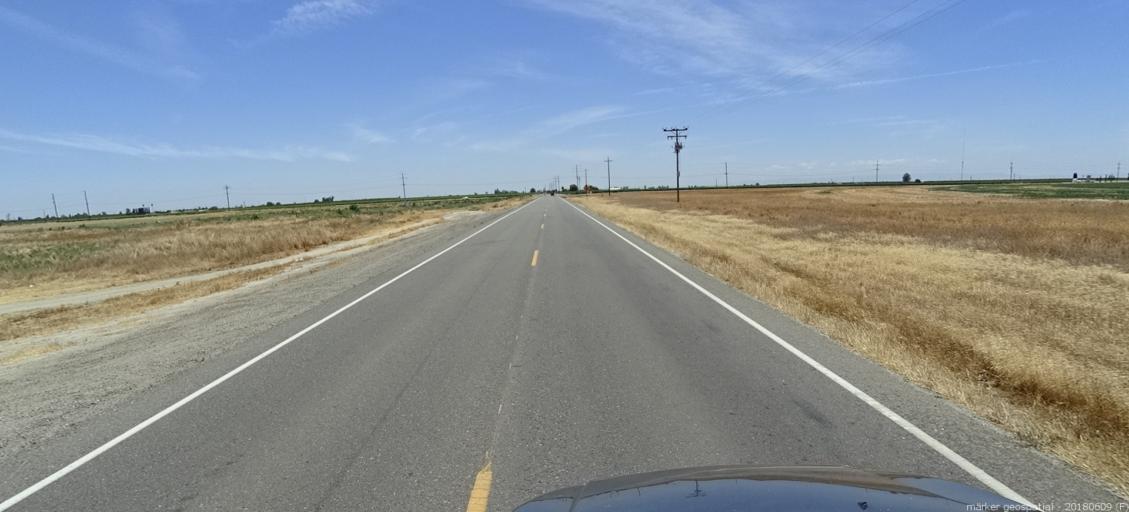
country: US
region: California
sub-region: Madera County
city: Madera
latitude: 36.9270
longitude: -120.1105
